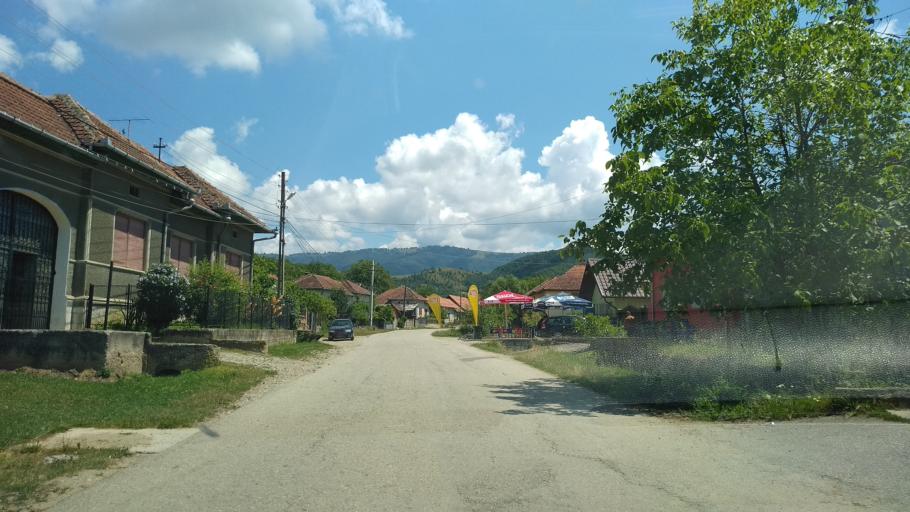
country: RO
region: Hunedoara
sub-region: Comuna Orastioara de Sus
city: Orastioara de Sus
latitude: 45.7105
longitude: 23.1281
